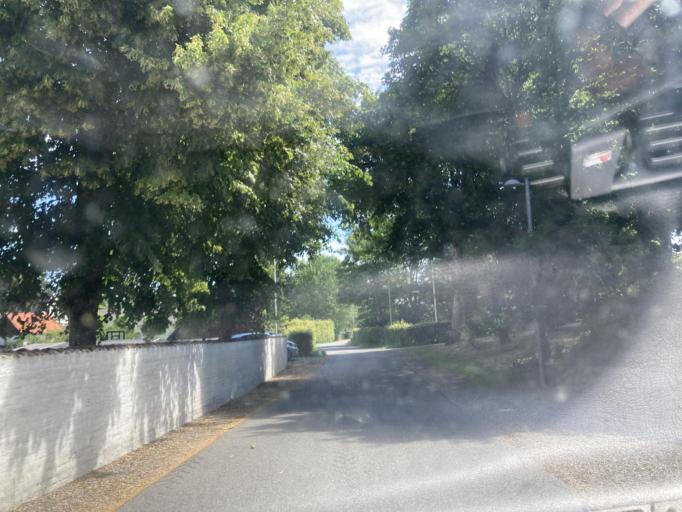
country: DK
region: Zealand
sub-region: Solrod Kommune
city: Solrod
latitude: 55.5266
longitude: 12.1623
